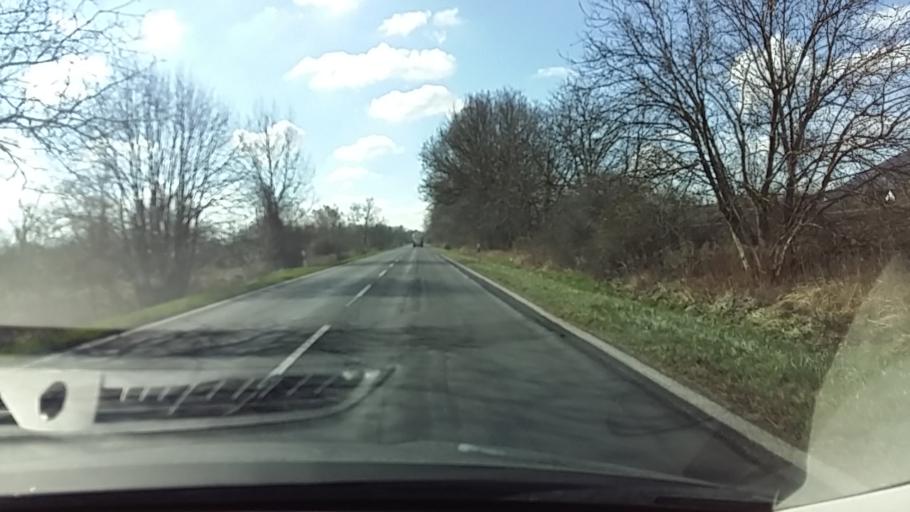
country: HU
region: Veszprem
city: Tapolca
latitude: 46.8186
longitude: 17.3816
